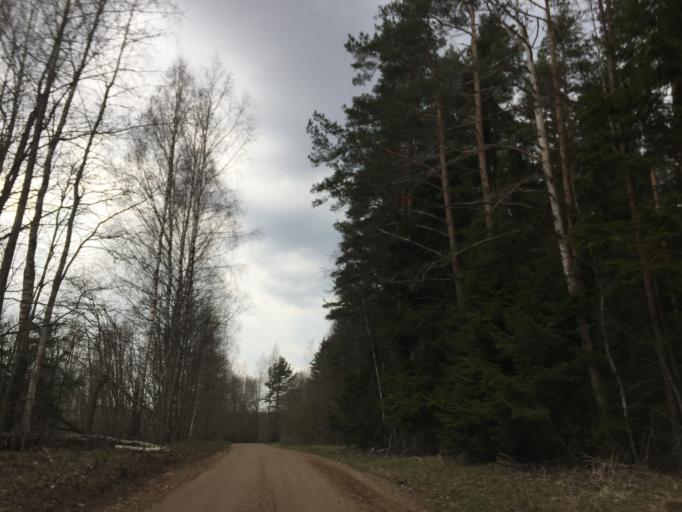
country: EE
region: Vorumaa
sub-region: Antsla vald
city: Vana-Antsla
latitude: 57.9422
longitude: 26.7219
